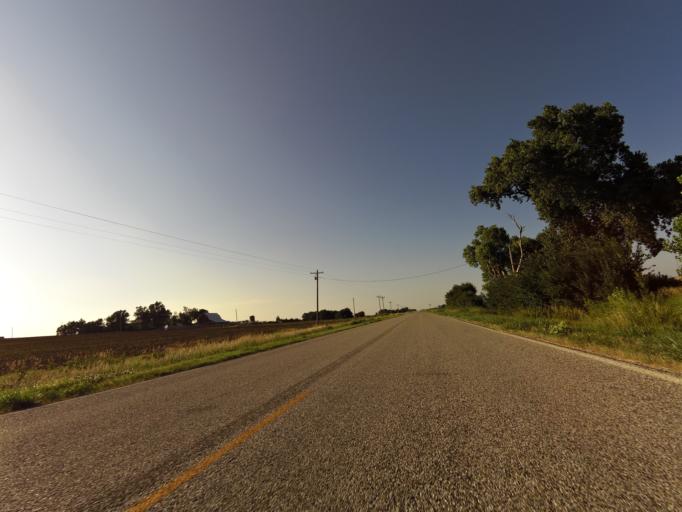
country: US
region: Kansas
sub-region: McPherson County
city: Inman
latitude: 38.1867
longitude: -97.8485
